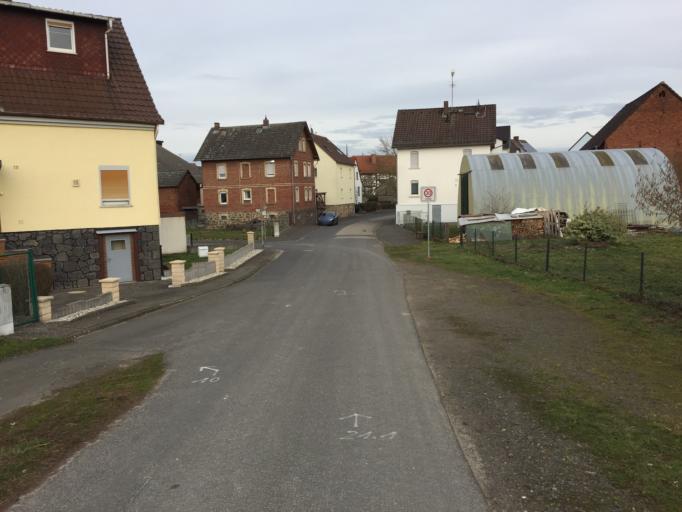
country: DE
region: Hesse
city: Staufenberg
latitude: 50.6654
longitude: 8.7838
